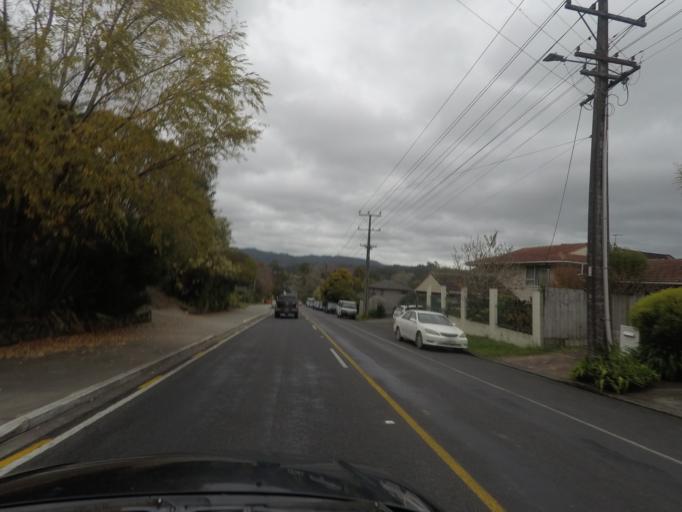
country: NZ
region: Auckland
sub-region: Auckland
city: Waitakere
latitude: -36.9090
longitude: 174.6260
